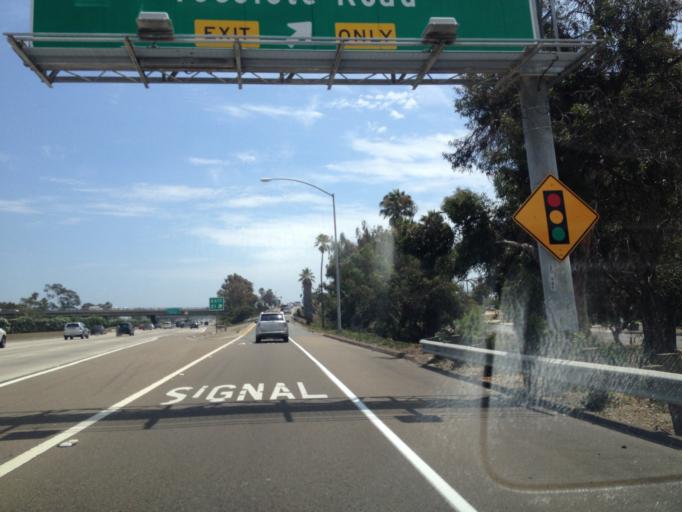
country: US
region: California
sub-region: San Diego County
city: San Diego
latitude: 32.7726
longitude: -117.2076
